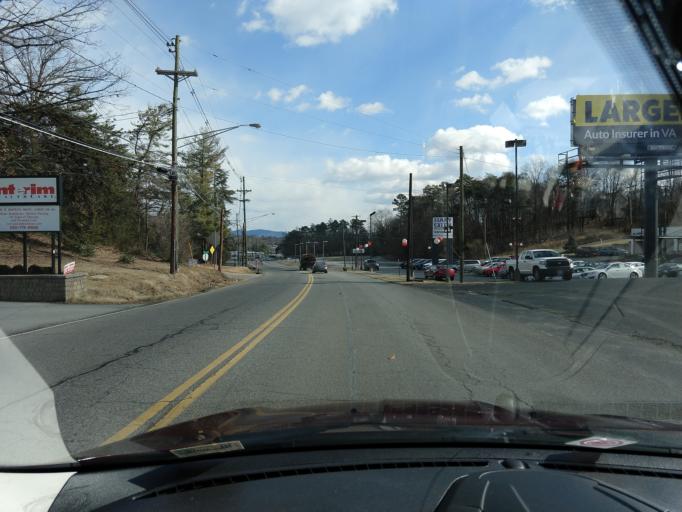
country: US
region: Virginia
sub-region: City of Salem
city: Salem
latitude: 37.2958
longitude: -80.0414
